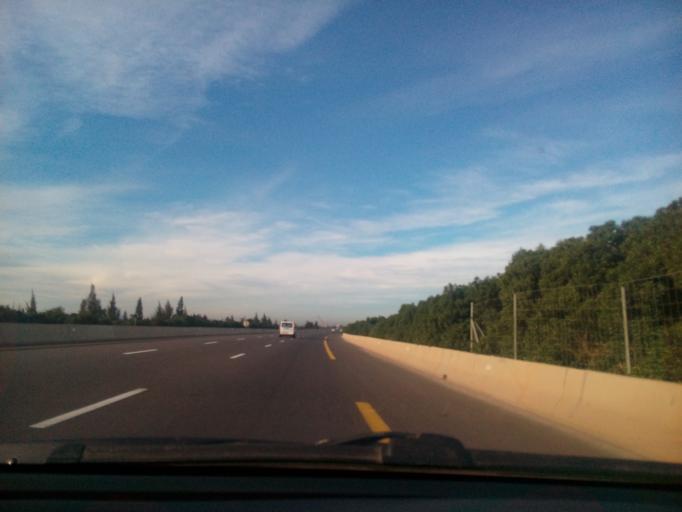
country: DZ
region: Mascara
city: Mascara
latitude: 35.6229
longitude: 0.0697
